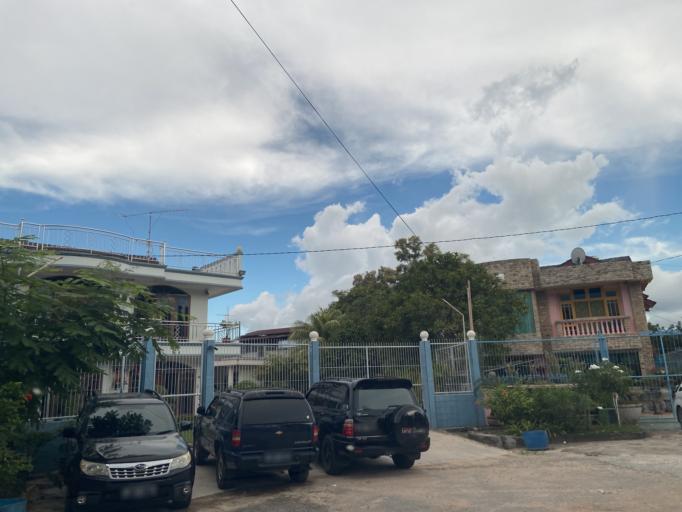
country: SG
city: Singapore
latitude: 1.1207
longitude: 104.0227
